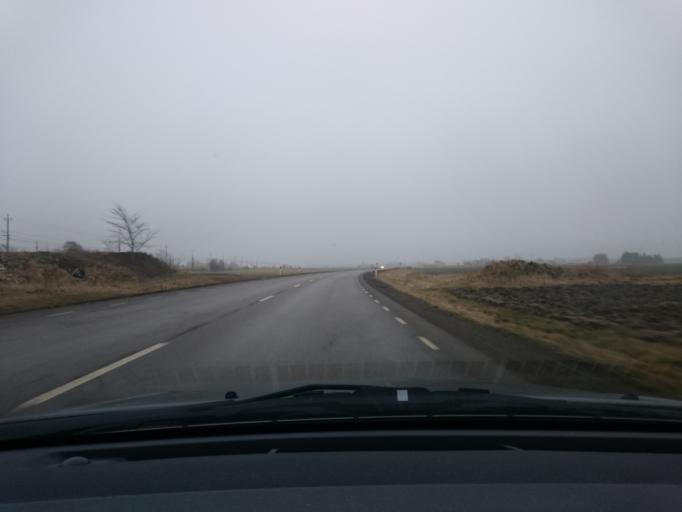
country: SE
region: Skane
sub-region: Bastads Kommun
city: Forslov
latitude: 56.3407
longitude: 12.8027
